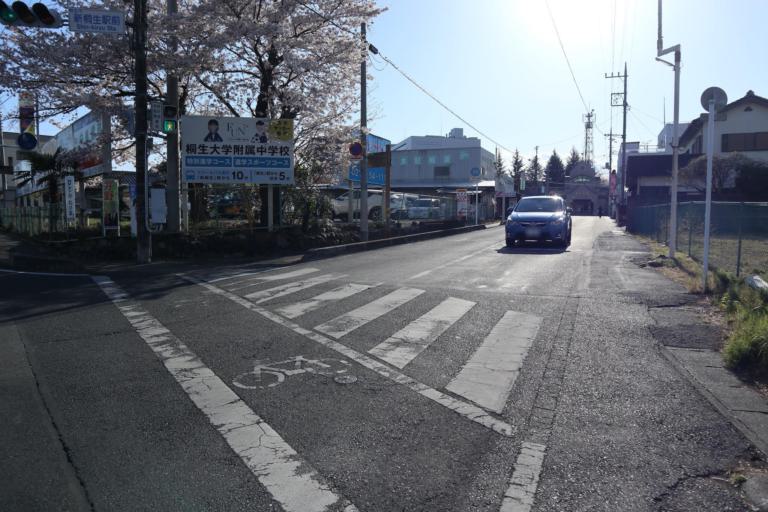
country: JP
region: Gunma
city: Kiryu
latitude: 36.3953
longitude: 139.3216
